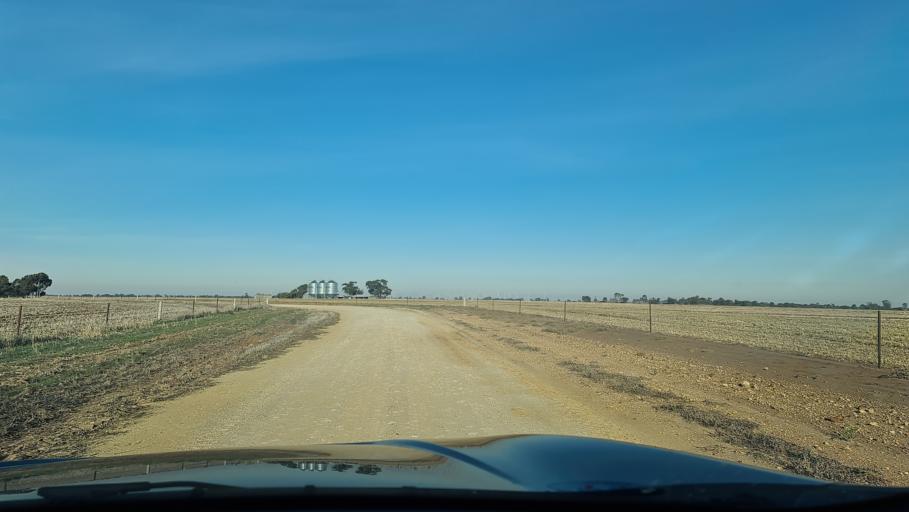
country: AU
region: Victoria
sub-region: Horsham
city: Horsham
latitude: -36.3614
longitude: 142.3963
